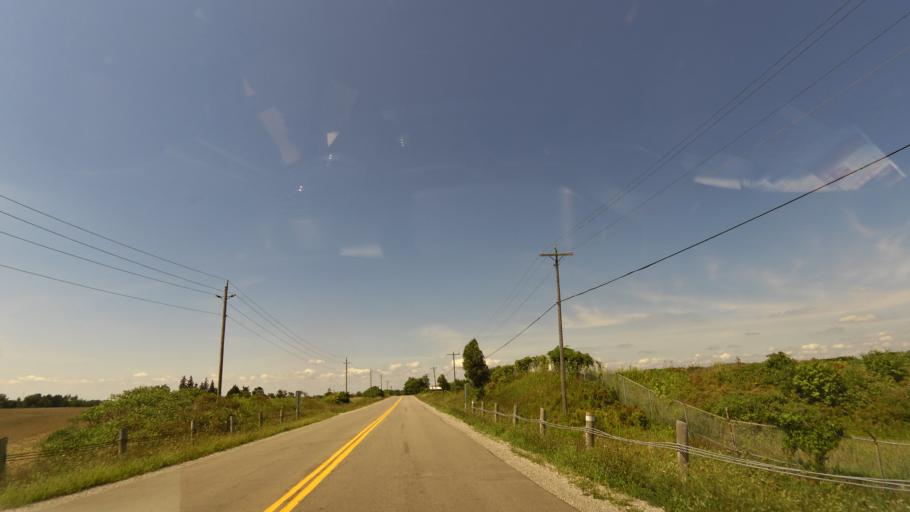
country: CA
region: Ontario
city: Ancaster
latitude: 43.1627
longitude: -79.9420
